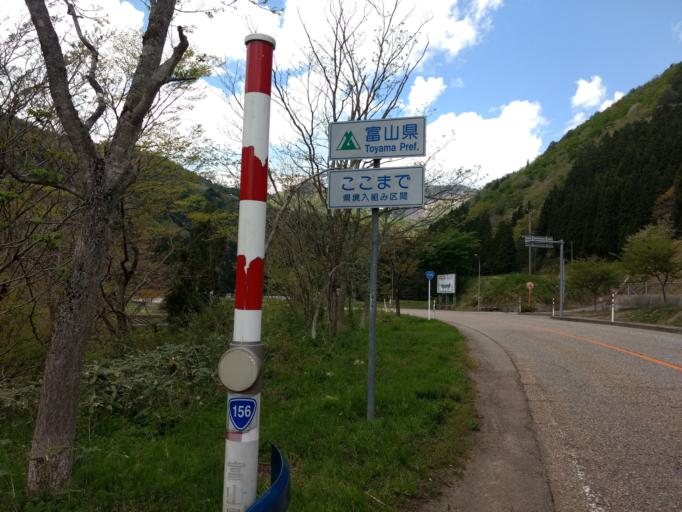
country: JP
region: Toyama
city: Fukumitsu
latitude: 36.3676
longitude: 136.8727
